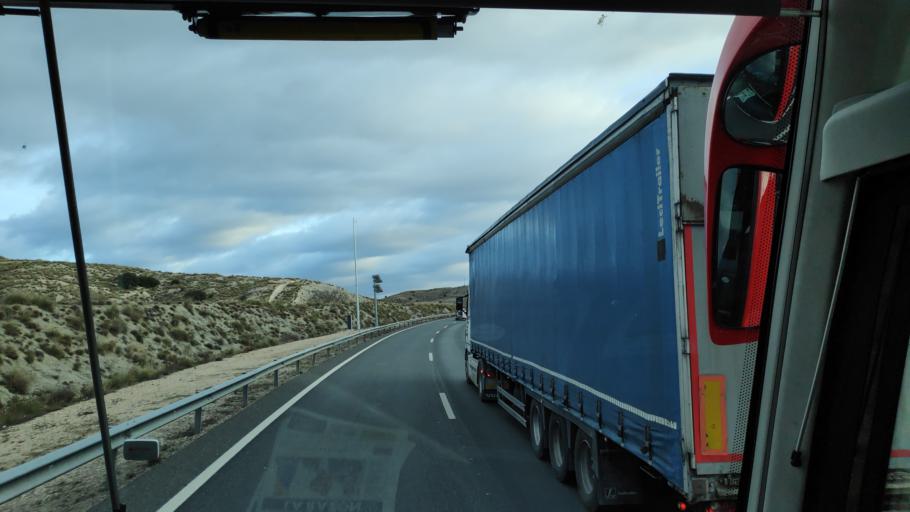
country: ES
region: Madrid
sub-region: Provincia de Madrid
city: Perales de Tajuna
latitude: 40.2133
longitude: -3.3263
